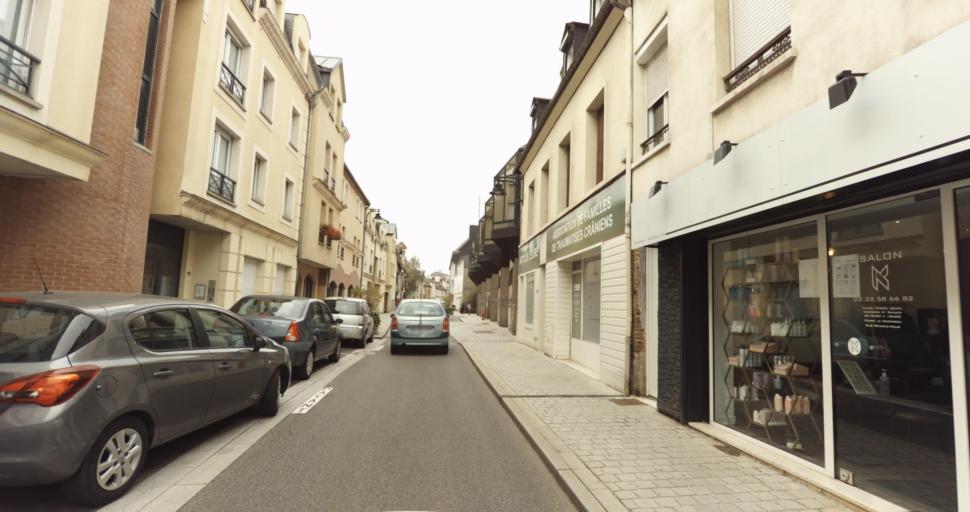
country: FR
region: Haute-Normandie
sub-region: Departement de l'Eure
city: Evreux
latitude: 49.0247
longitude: 1.1451
